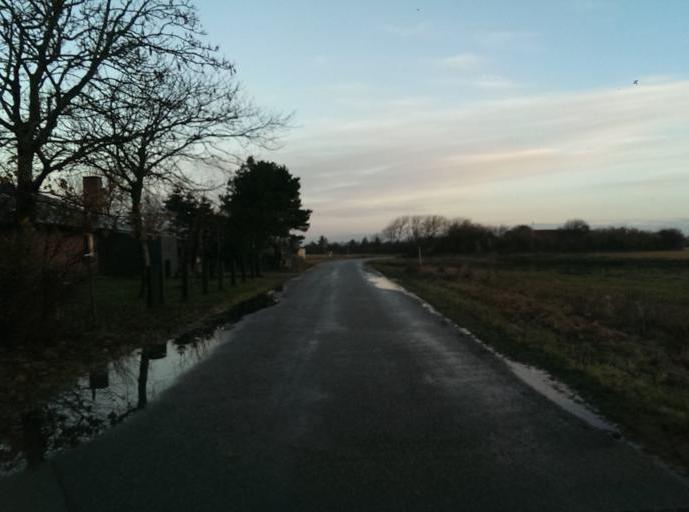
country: DK
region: South Denmark
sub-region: Esbjerg Kommune
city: Tjaereborg
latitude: 55.4661
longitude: 8.6298
